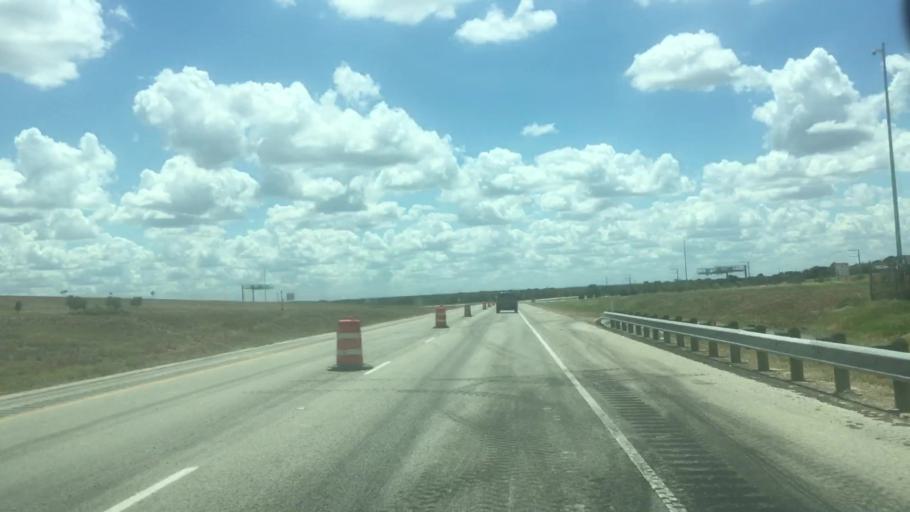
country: US
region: Texas
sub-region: Caldwell County
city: Martindale
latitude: 29.7841
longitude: -97.7882
